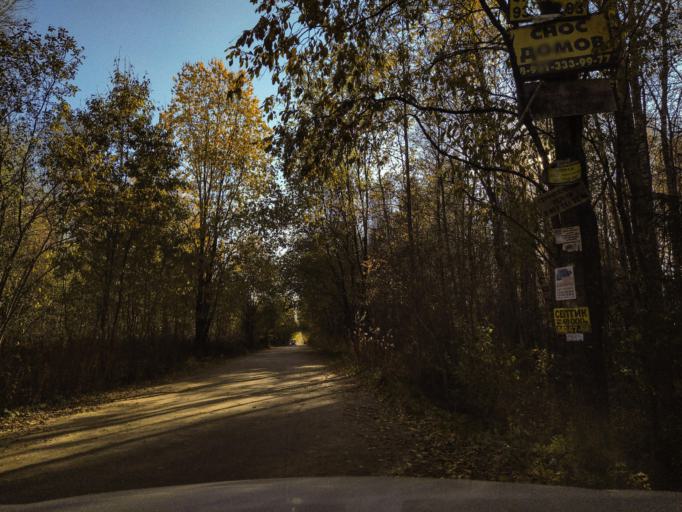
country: RU
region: Leningrad
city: Siverskiy
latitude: 59.2984
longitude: 30.0347
